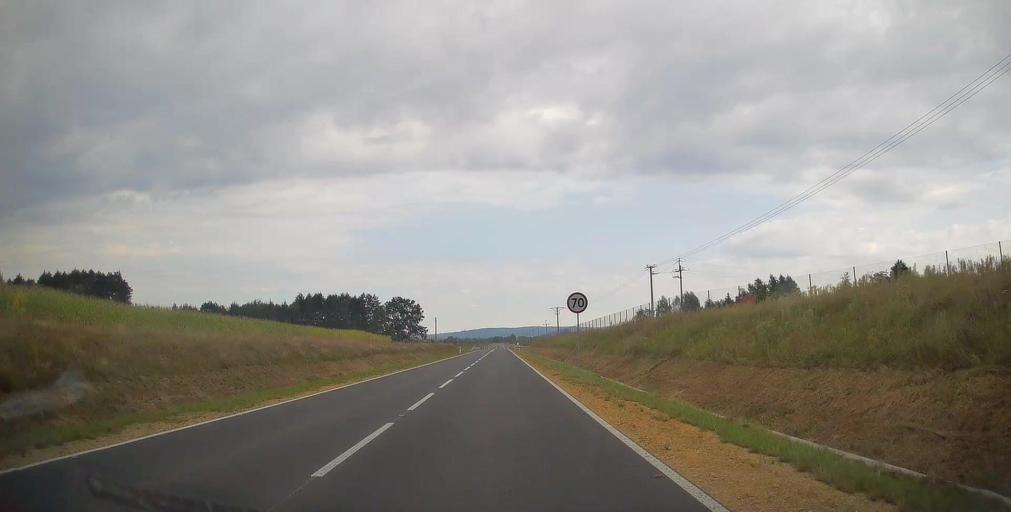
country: PL
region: Lesser Poland Voivodeship
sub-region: Powiat oswiecimski
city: Zator
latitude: 50.0093
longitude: 19.4248
